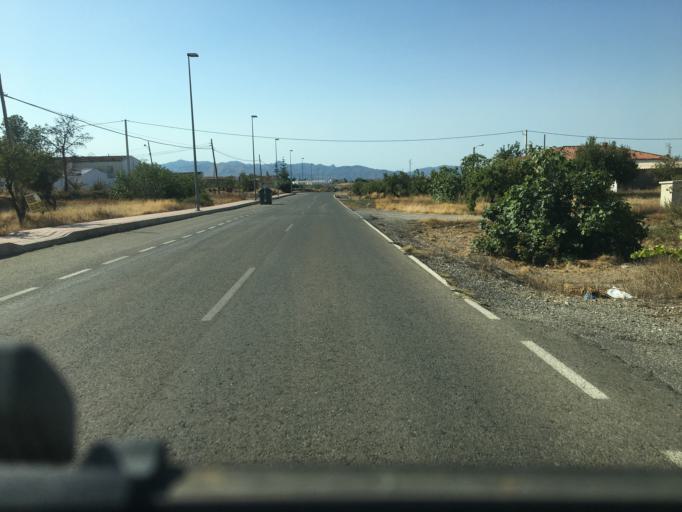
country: ES
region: Andalusia
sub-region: Provincia de Almeria
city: Huercal-Overa
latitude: 37.4477
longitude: -1.9837
